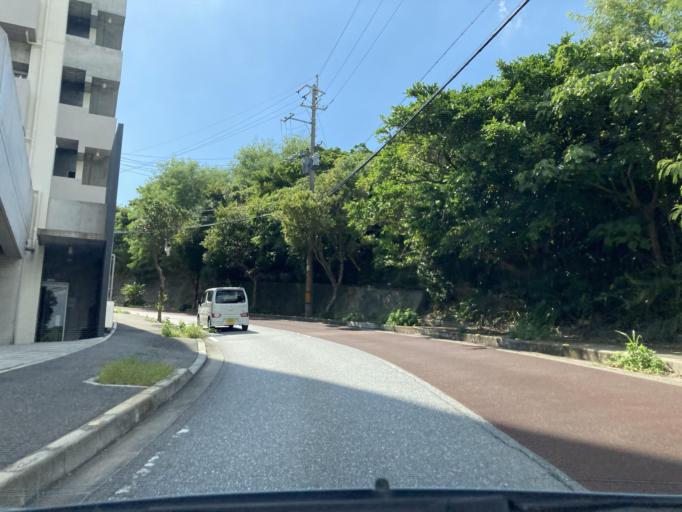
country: JP
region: Okinawa
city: Ginowan
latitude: 26.2462
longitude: 127.7563
